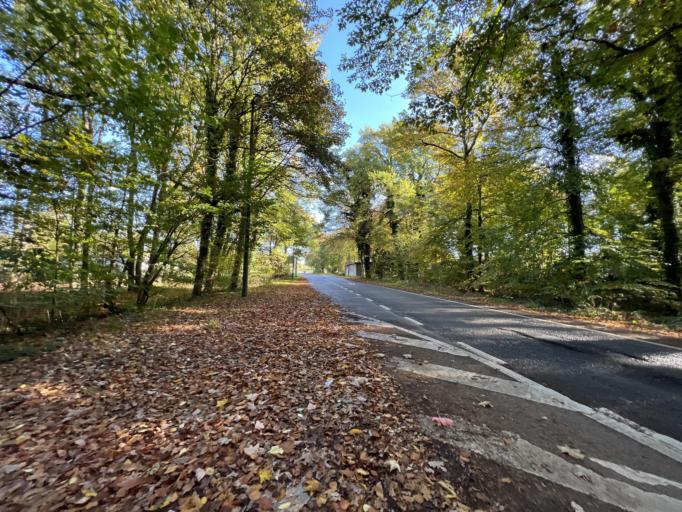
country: BE
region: Wallonia
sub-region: Province de Liege
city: Esneux
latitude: 50.5847
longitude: 5.5611
